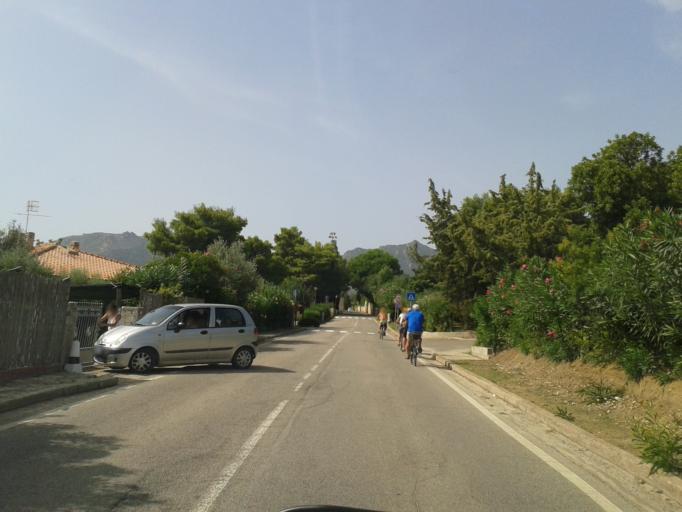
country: IT
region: Sardinia
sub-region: Provincia di Cagliari
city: Villasimius
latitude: 39.1302
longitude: 9.5082
